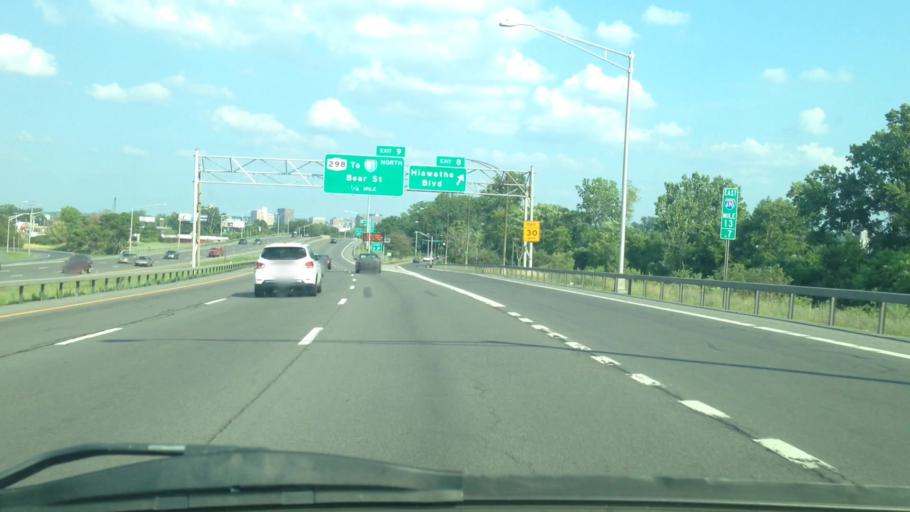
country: US
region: New York
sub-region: Onondaga County
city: Solvay
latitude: 43.0596
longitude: -76.1861
